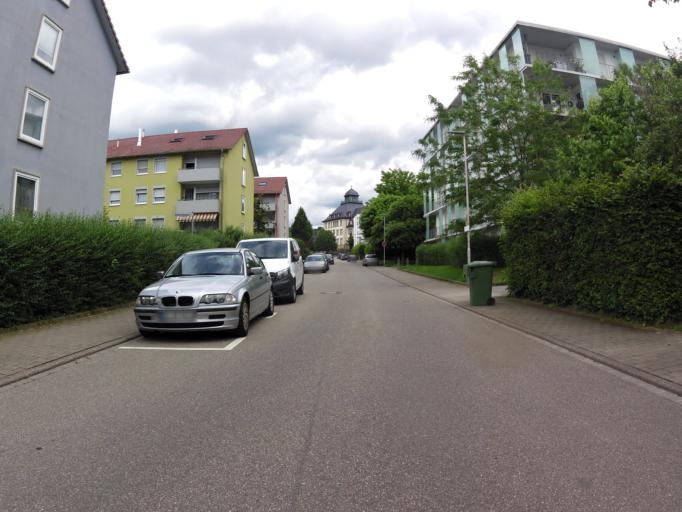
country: DE
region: Baden-Wuerttemberg
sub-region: Freiburg Region
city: Lahr
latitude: 48.3434
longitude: 7.8798
